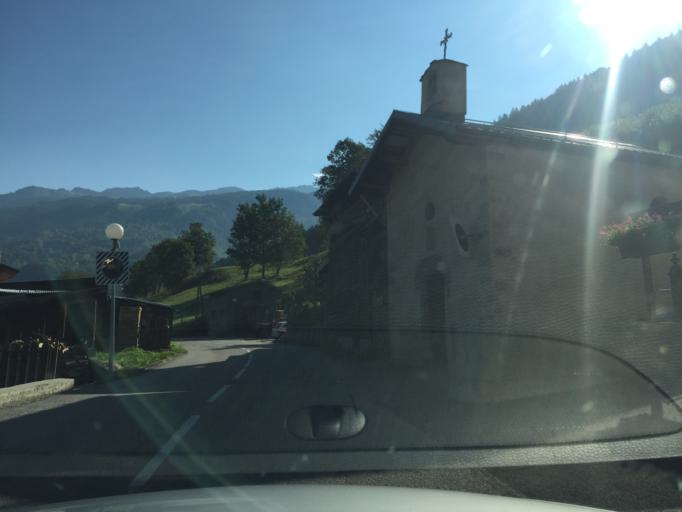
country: FR
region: Rhone-Alpes
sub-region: Departement de la Savoie
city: Macot-la-Plagne
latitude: 45.5679
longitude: 6.7226
